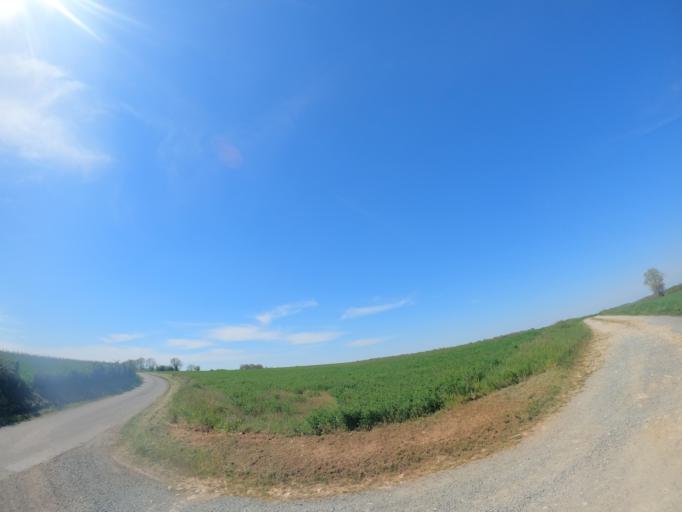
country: FR
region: Poitou-Charentes
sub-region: Departement des Deux-Sevres
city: Airvault
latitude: 46.8875
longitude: -0.1437
